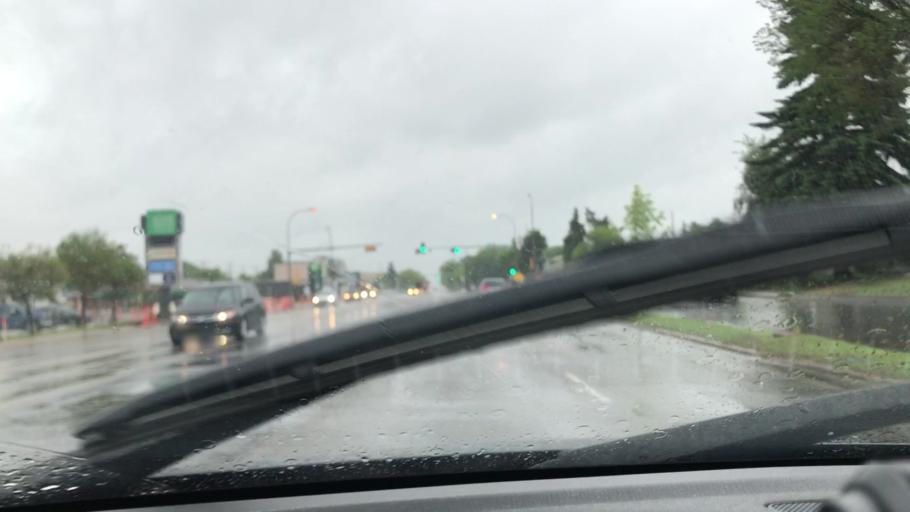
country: CA
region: Alberta
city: Edmonton
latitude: 53.5180
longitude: -113.4569
